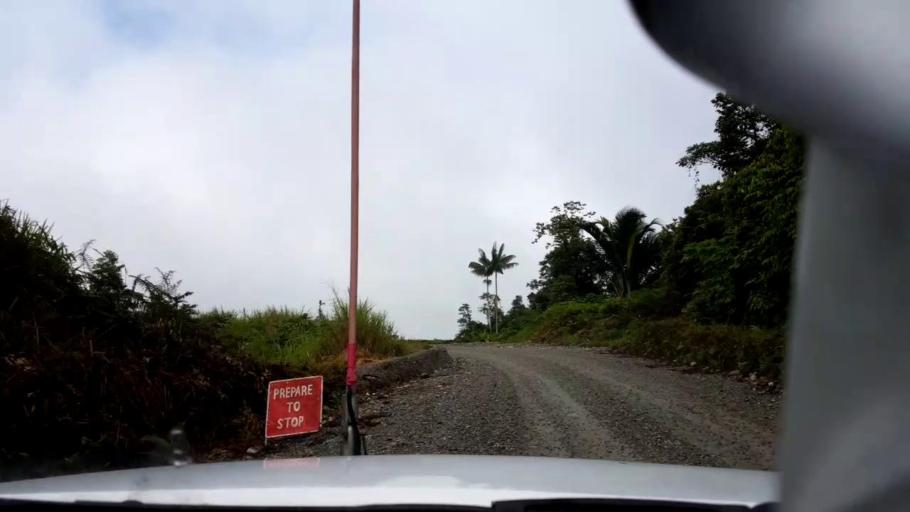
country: PG
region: Western Province
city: Kiunga
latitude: -5.5241
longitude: 141.2783
